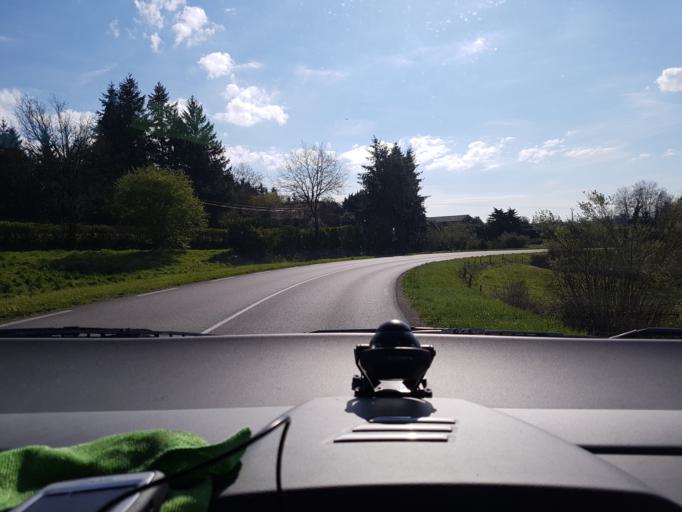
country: FR
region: Midi-Pyrenees
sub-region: Departement de l'Aveyron
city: Colombies
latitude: 44.4026
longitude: 2.3551
